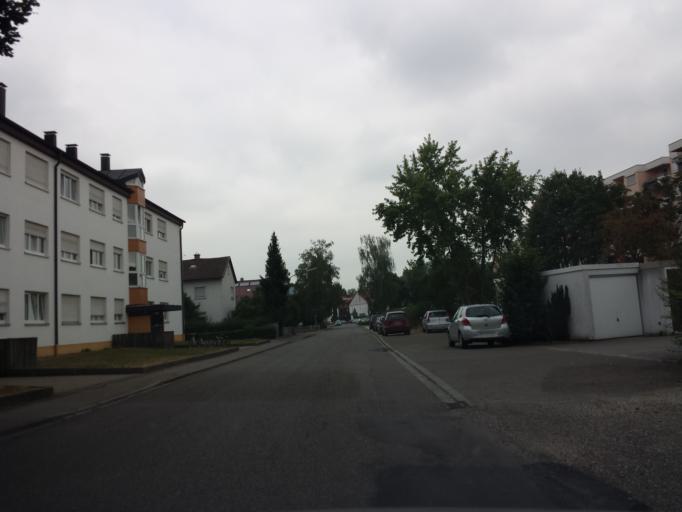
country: DE
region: Bavaria
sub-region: Swabia
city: Wasserburg
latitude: 48.4451
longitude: 10.2700
